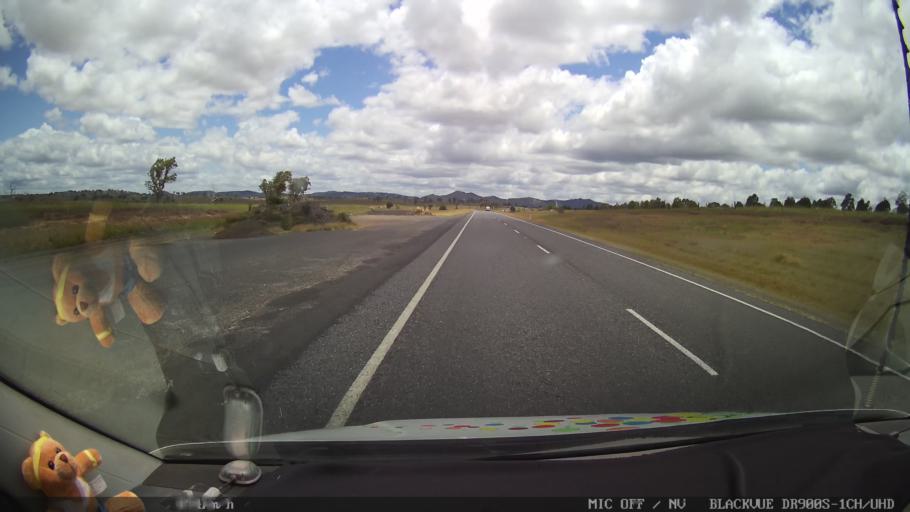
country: AU
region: New South Wales
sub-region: Glen Innes Severn
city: Glen Innes
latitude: -29.4040
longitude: 151.8719
